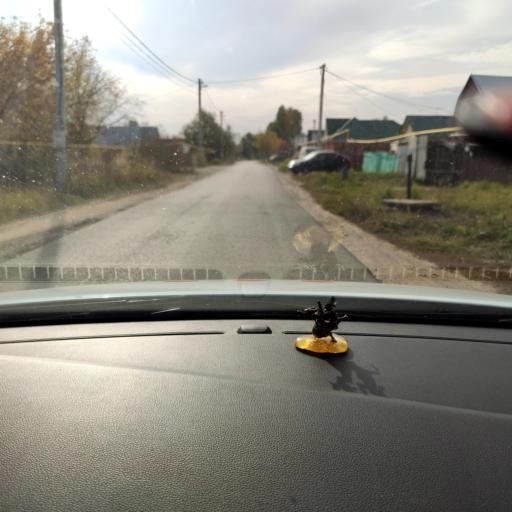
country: RU
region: Tatarstan
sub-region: Gorod Kazan'
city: Kazan
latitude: 55.7513
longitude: 49.1146
